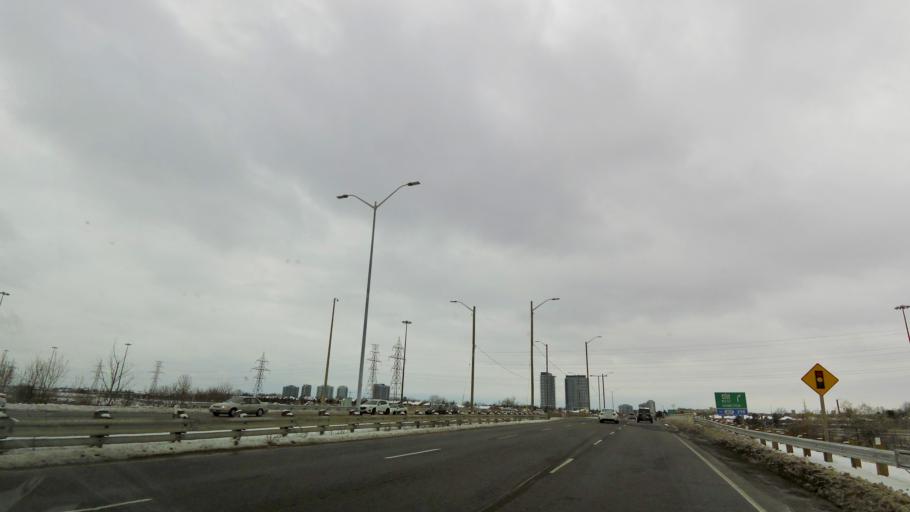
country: CA
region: Ontario
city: Mississauga
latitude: 43.5537
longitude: -79.6954
